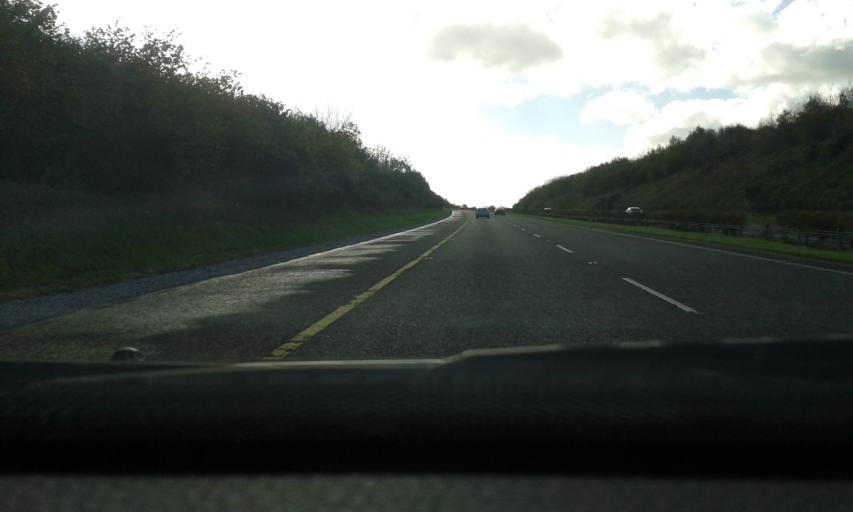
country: IE
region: Munster
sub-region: County Cork
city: Watergrasshill
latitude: 51.9869
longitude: -8.3633
